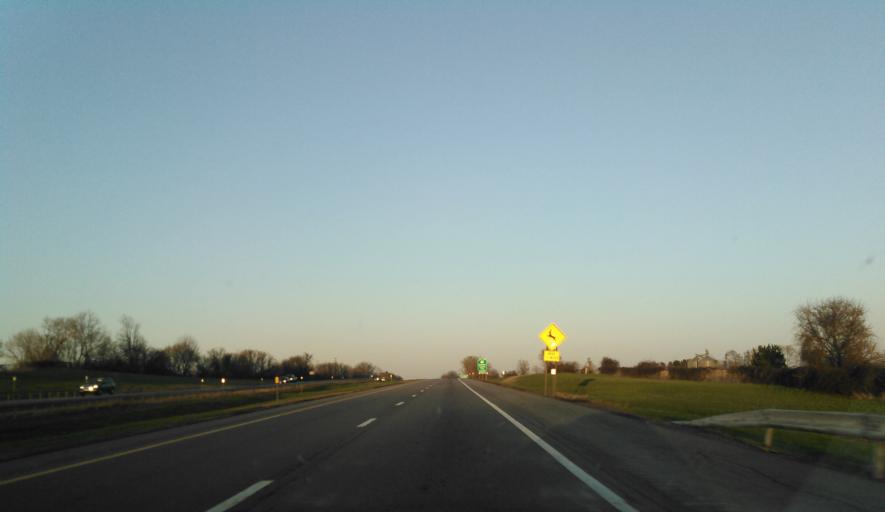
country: US
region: New York
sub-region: Ontario County
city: Phelps
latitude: 42.9553
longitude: -77.0117
